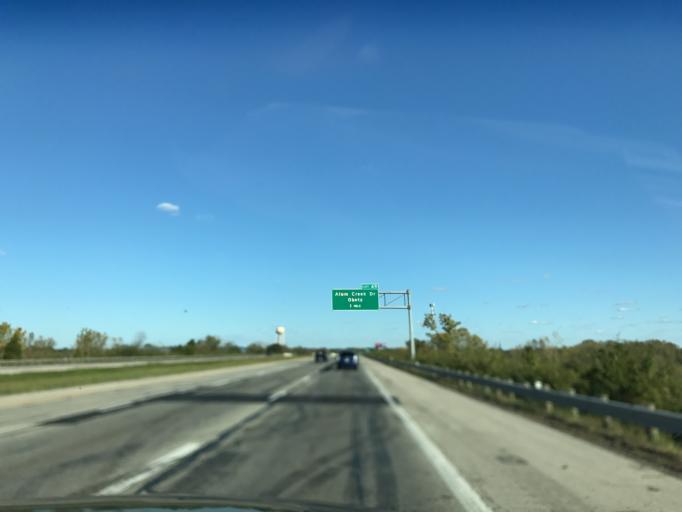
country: US
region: Ohio
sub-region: Franklin County
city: Obetz
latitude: 39.8720
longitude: -82.9559
